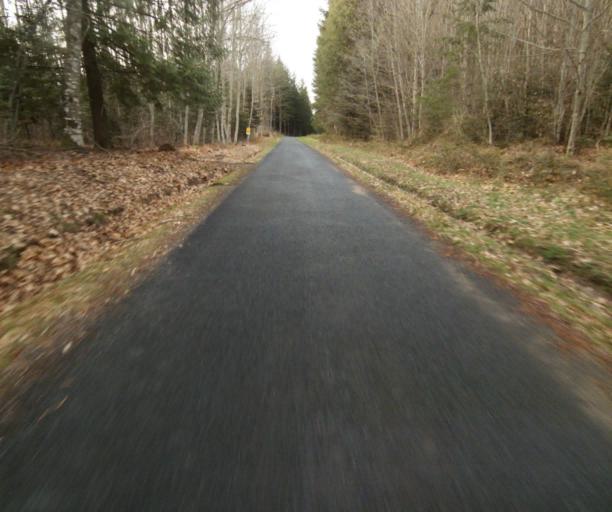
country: FR
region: Limousin
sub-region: Departement de la Correze
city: Argentat
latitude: 45.2134
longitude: 1.9433
